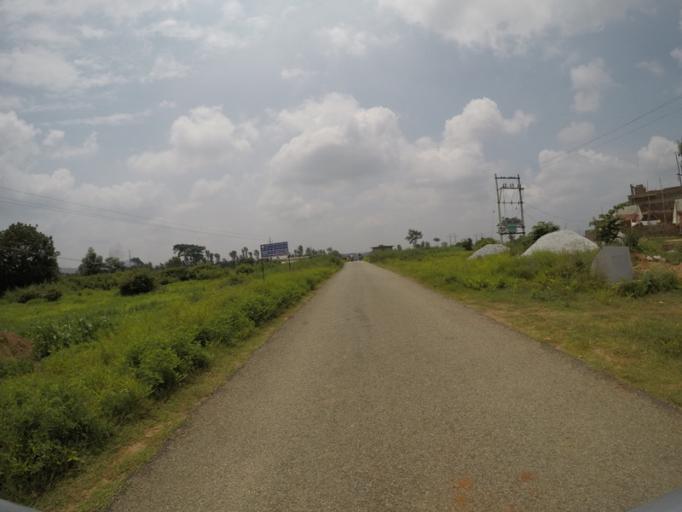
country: IN
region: Karnataka
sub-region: Ramanagara
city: Kanakapura
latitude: 12.7193
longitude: 77.4800
